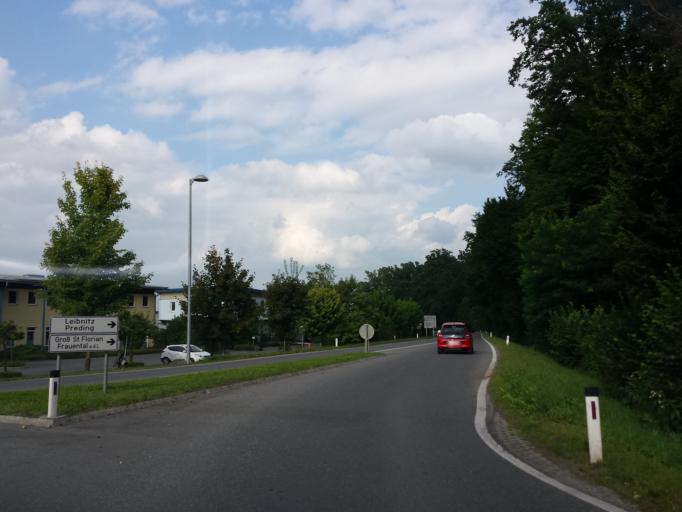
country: AT
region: Styria
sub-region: Politischer Bezirk Deutschlandsberg
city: Deutschlandsberg
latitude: 46.8160
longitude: 15.2431
